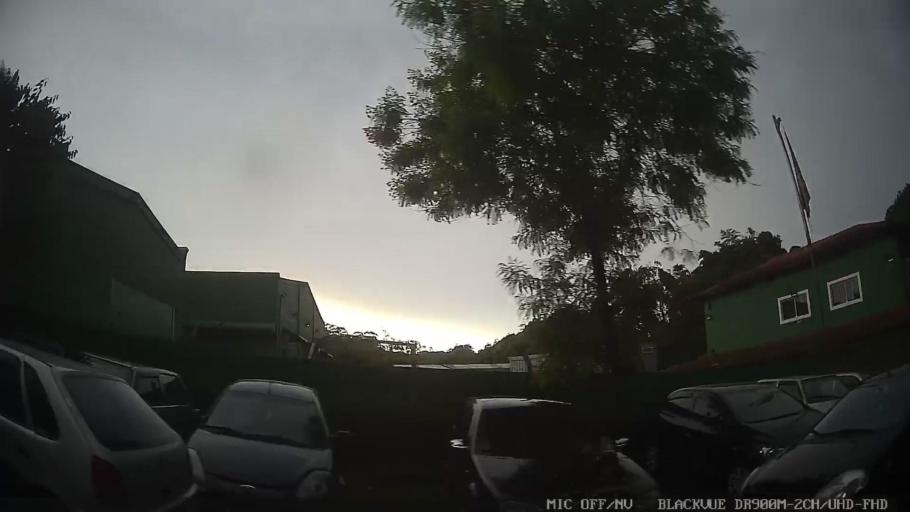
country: BR
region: Sao Paulo
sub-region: Ribeirao Pires
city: Ribeirao Pires
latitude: -23.6936
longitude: -46.3653
